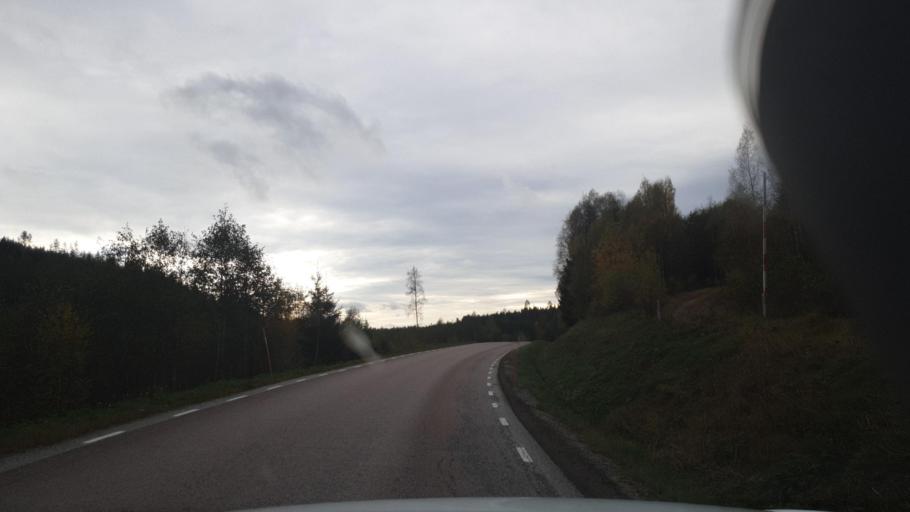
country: SE
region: Vaermland
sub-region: Arvika Kommun
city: Arvika
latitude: 59.7122
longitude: 12.7953
